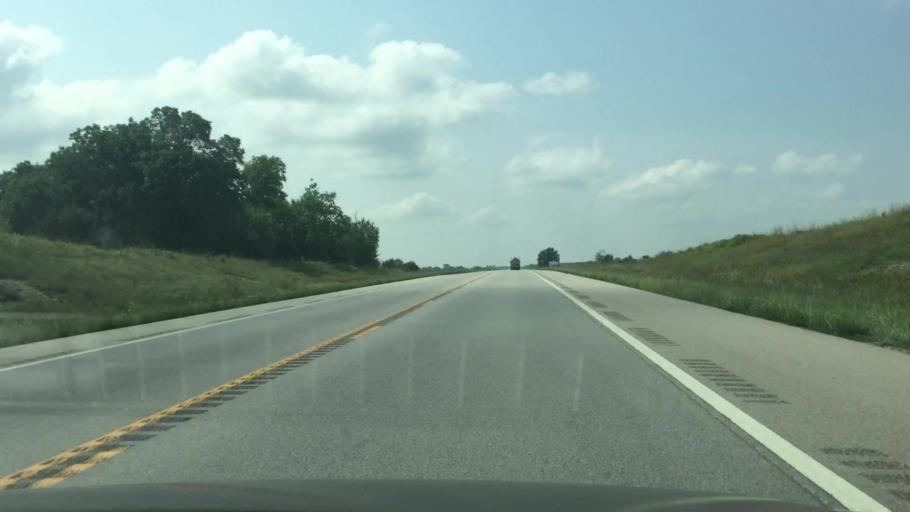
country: US
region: Kansas
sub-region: Allen County
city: Iola
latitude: 37.9719
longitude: -95.3807
